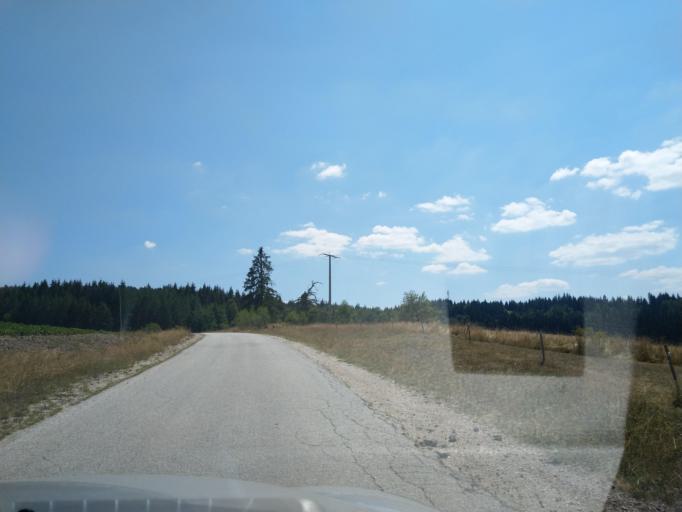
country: RS
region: Central Serbia
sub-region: Zlatiborski Okrug
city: Nova Varos
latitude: 43.4701
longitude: 19.9662
